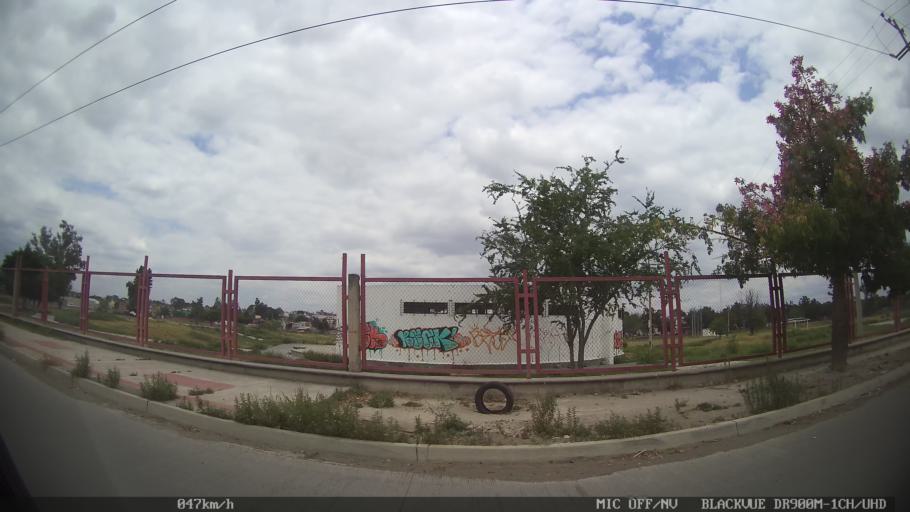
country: MX
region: Jalisco
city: Tlaquepaque
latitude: 20.6521
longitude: -103.2695
